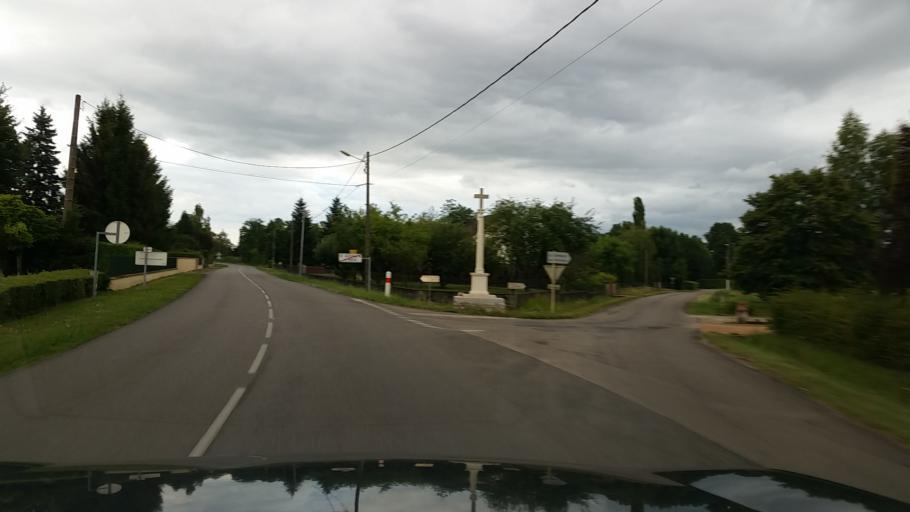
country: FR
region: Bourgogne
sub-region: Departement de Saone-et-Loire
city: Saint-Germain-du-Bois
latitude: 46.7449
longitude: 5.2461
